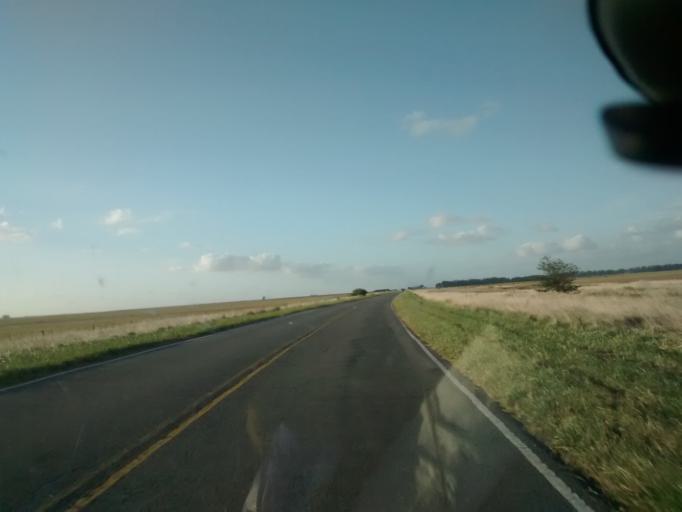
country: AR
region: Buenos Aires
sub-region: Partido de General Belgrano
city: General Belgrano
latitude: -36.0674
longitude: -58.6257
